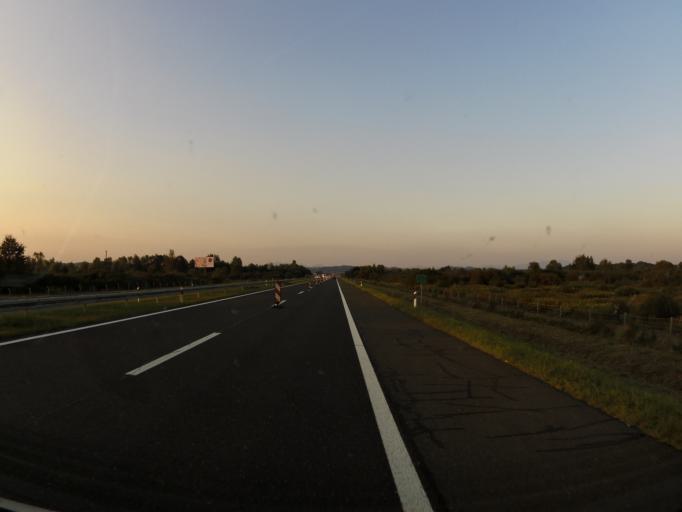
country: HR
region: Zagrebacka
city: Jakovlje
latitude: 45.9820
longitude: 15.8569
